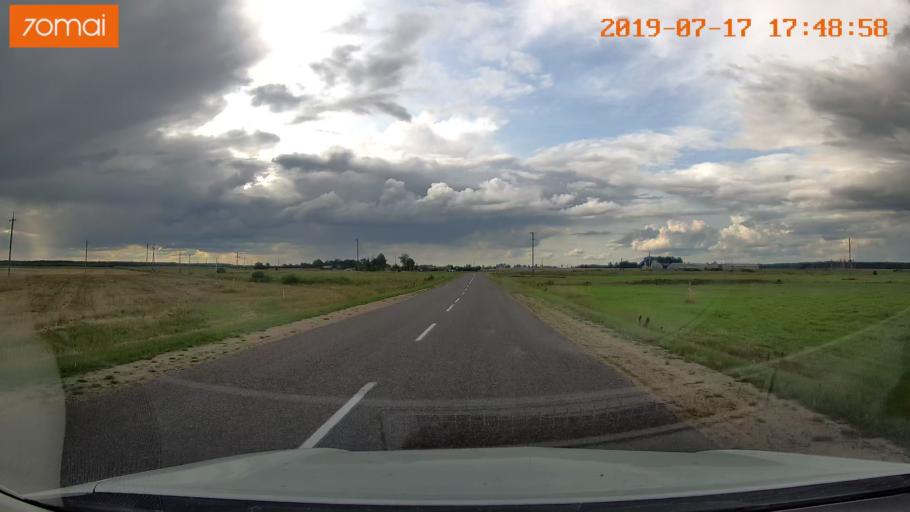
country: BY
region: Mogilev
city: Hlusha
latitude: 53.1280
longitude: 28.8186
